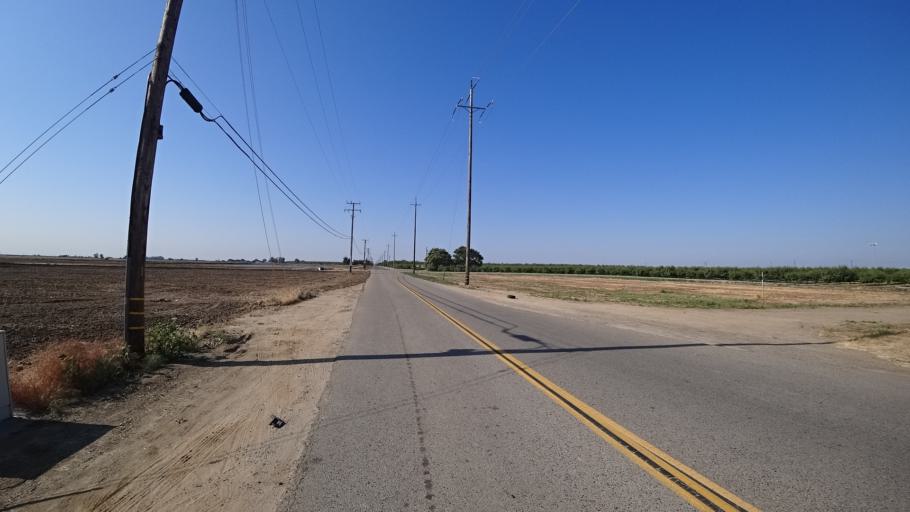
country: US
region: California
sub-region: Kings County
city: Home Garden
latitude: 36.3275
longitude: -119.5831
